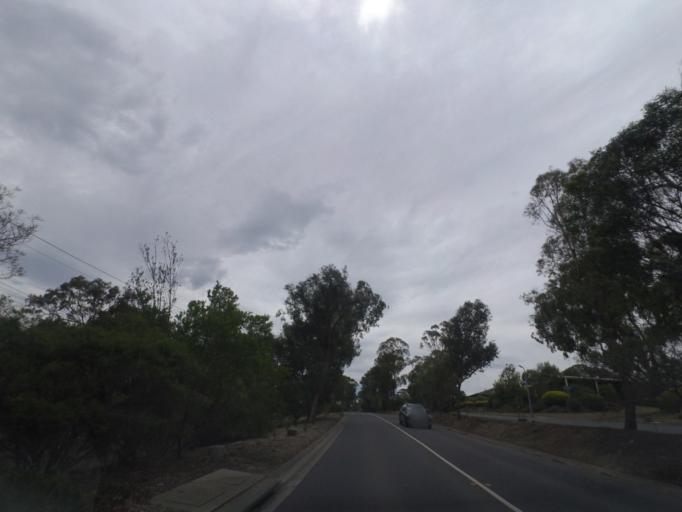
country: AU
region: Victoria
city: Saint Helena
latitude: -37.6967
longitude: 145.1255
